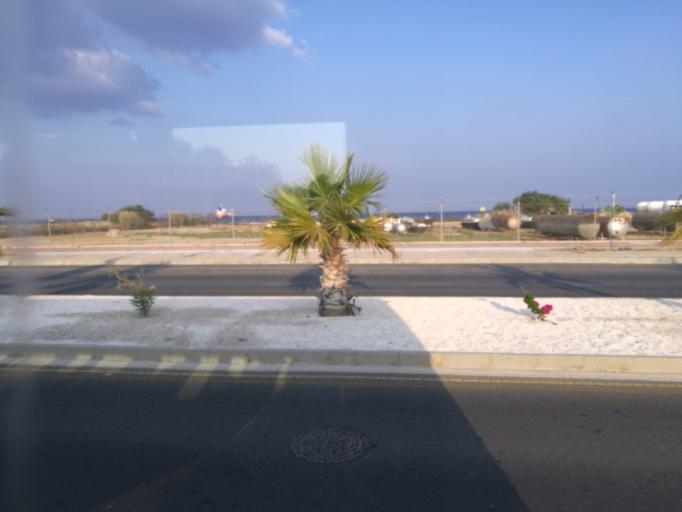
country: CY
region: Larnaka
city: Livadia
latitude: 34.9461
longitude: 33.6448
